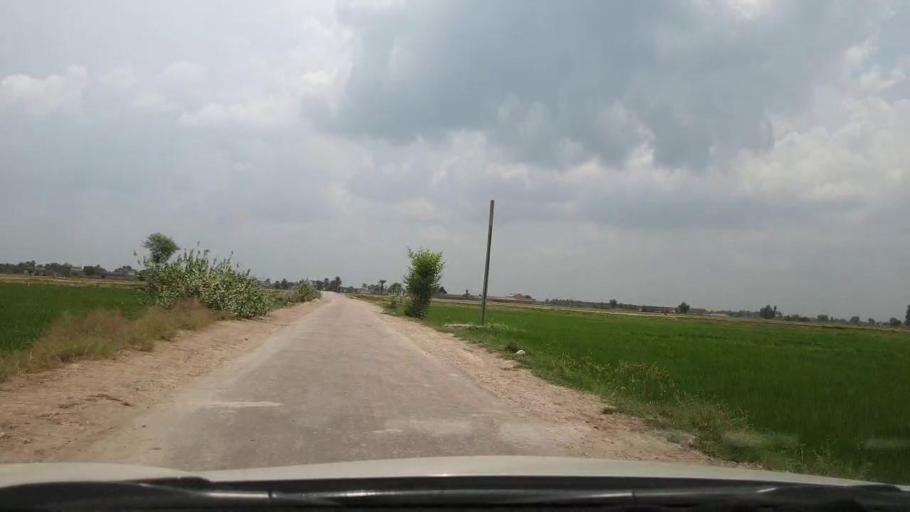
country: PK
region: Sindh
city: Goth Garelo
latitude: 27.4257
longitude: 68.1085
